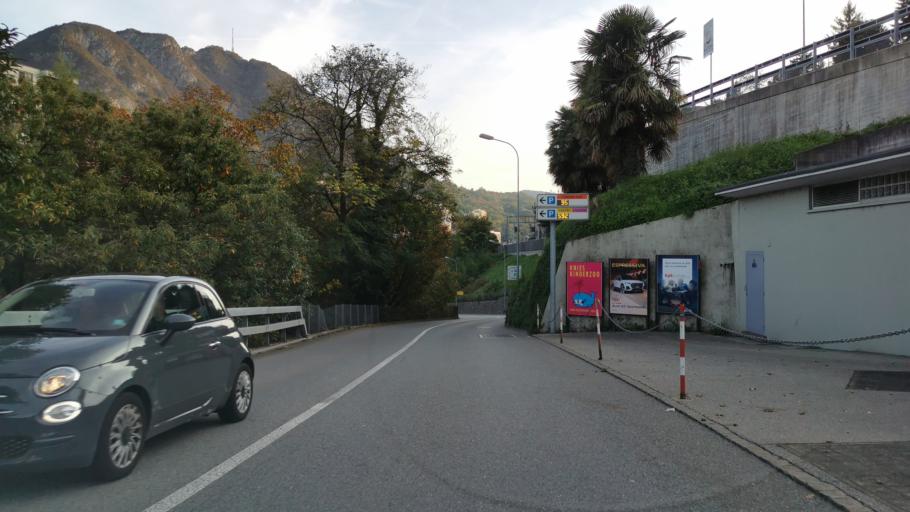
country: CH
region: Ticino
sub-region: Lugano District
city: Sorengo
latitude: 45.9963
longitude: 8.9428
